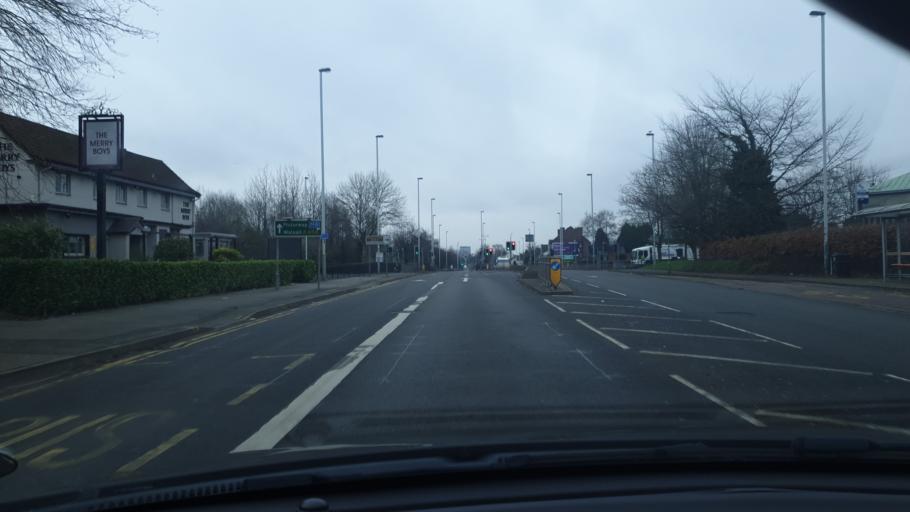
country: GB
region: England
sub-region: Wolverhampton
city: Wednesfield
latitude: 52.5837
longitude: -2.0868
